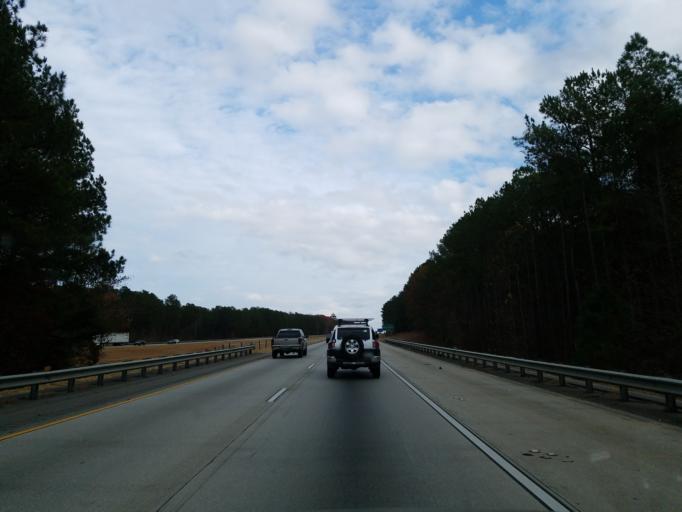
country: US
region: Georgia
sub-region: Carroll County
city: Mount Zion
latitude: 33.6895
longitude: -85.2035
